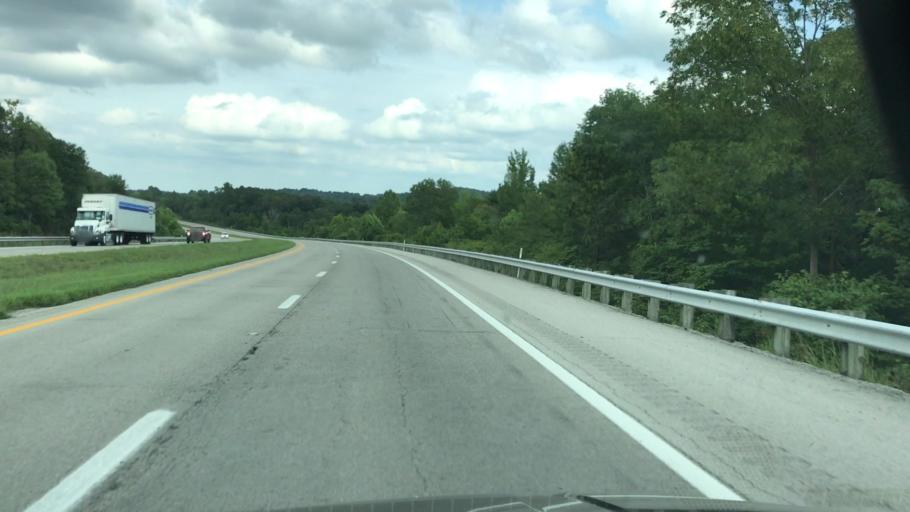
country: US
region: Kentucky
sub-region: Caldwell County
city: Princeton
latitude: 37.1412
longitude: -87.8103
